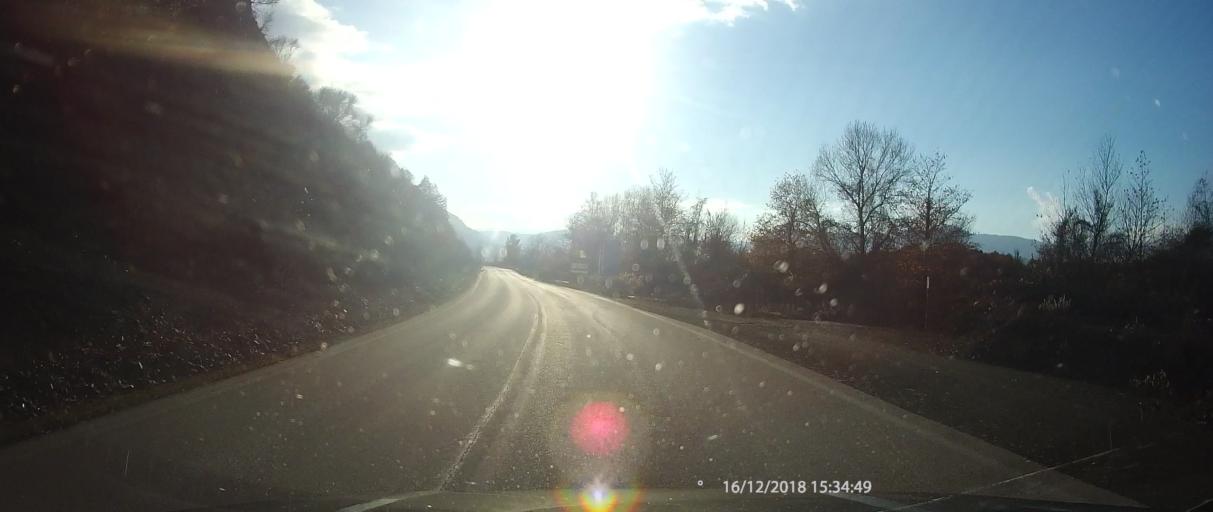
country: GR
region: Epirus
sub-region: Nomos Ioanninon
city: Konitsa
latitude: 40.0570
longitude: 20.7372
